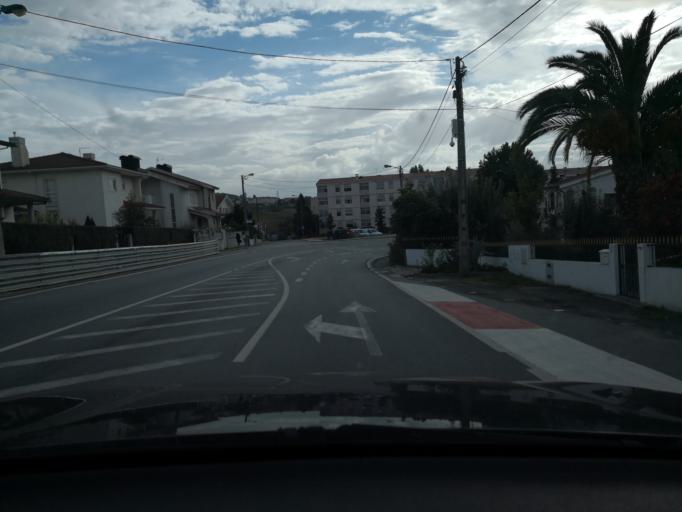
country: PT
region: Vila Real
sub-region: Vila Real
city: Vila Real
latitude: 41.2951
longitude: -7.7290
